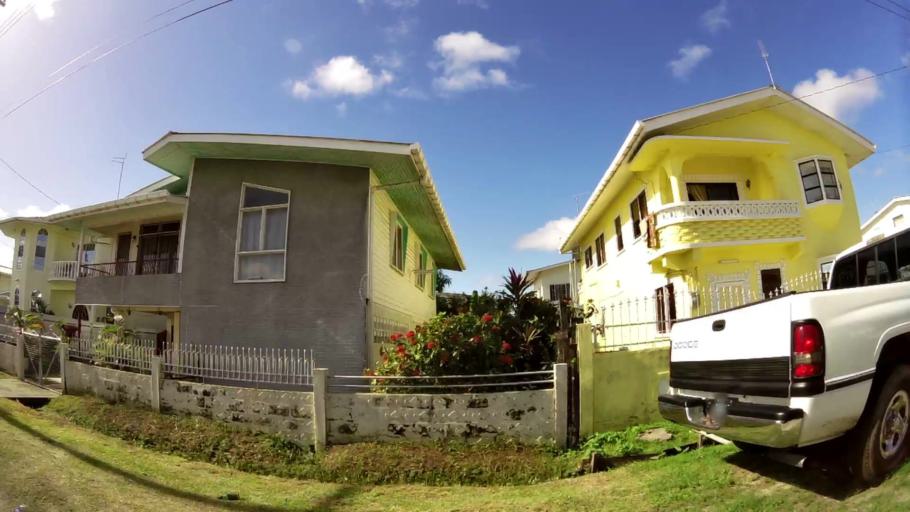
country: GY
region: Demerara-Mahaica
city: Georgetown
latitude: 6.8169
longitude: -58.1294
